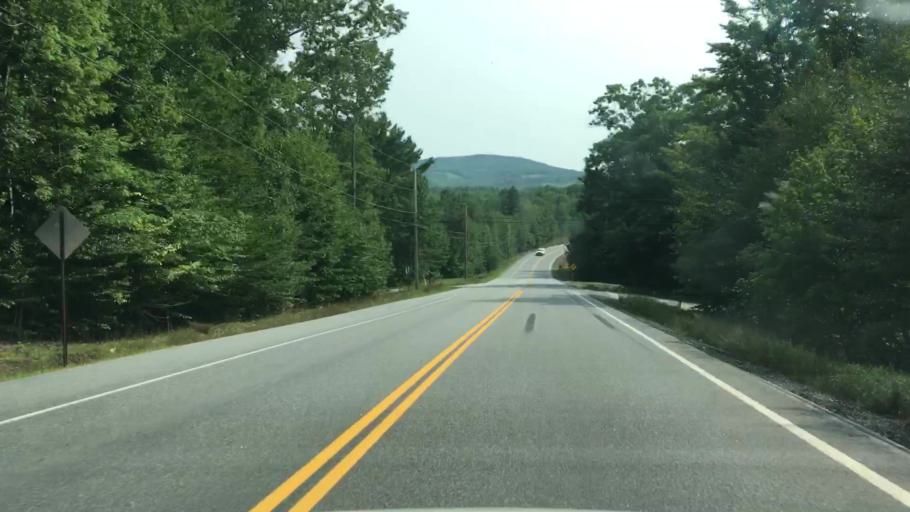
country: US
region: Maine
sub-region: Oxford County
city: Paris
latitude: 44.2530
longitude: -70.4381
